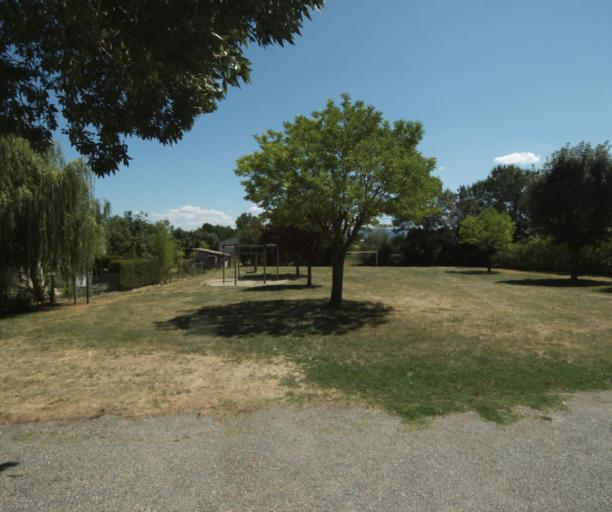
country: FR
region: Midi-Pyrenees
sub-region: Departement de la Haute-Garonne
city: Saint-Felix-Lauragais
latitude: 43.4632
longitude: 1.9293
